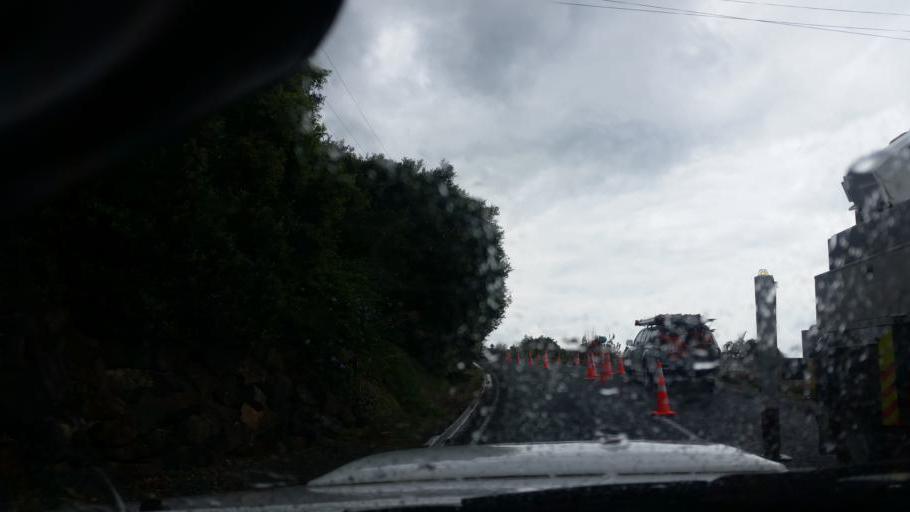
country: NZ
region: Auckland
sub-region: Auckland
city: Wellsford
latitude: -36.1567
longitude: 174.2275
